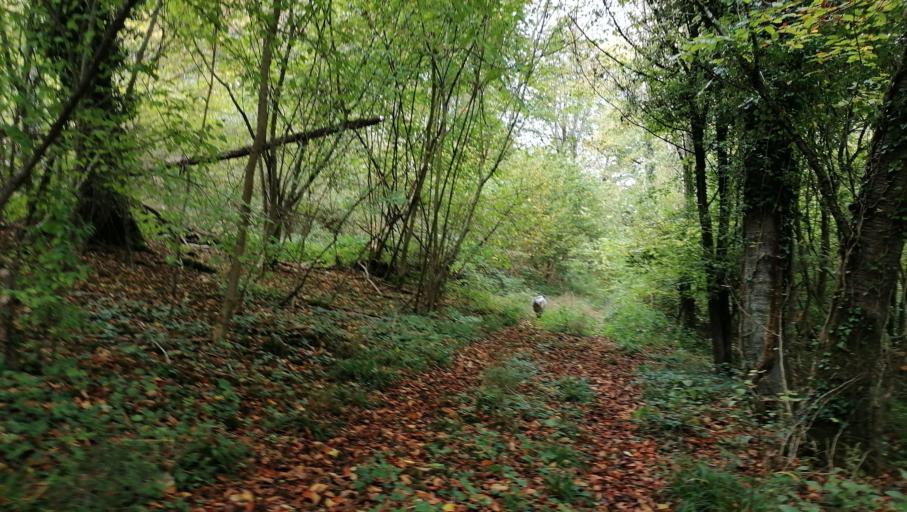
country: FR
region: Picardie
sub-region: Departement de la Somme
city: Bouttencourt
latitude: 49.8921
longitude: 1.6788
